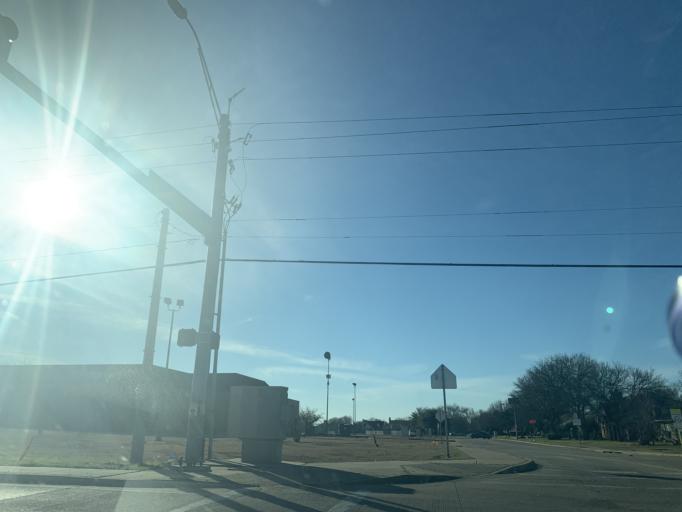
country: US
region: Texas
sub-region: Dallas County
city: Cedar Hill
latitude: 32.5899
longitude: -96.9335
